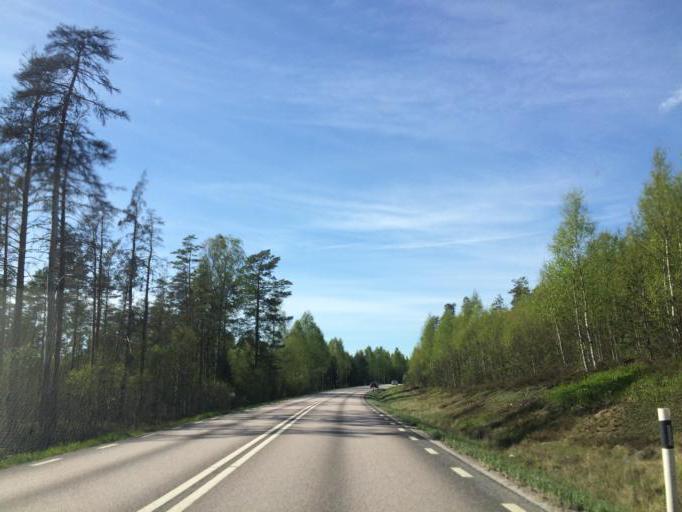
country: SE
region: Soedermanland
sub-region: Katrineholms Kommun
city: Katrineholm
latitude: 59.1147
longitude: 16.1670
